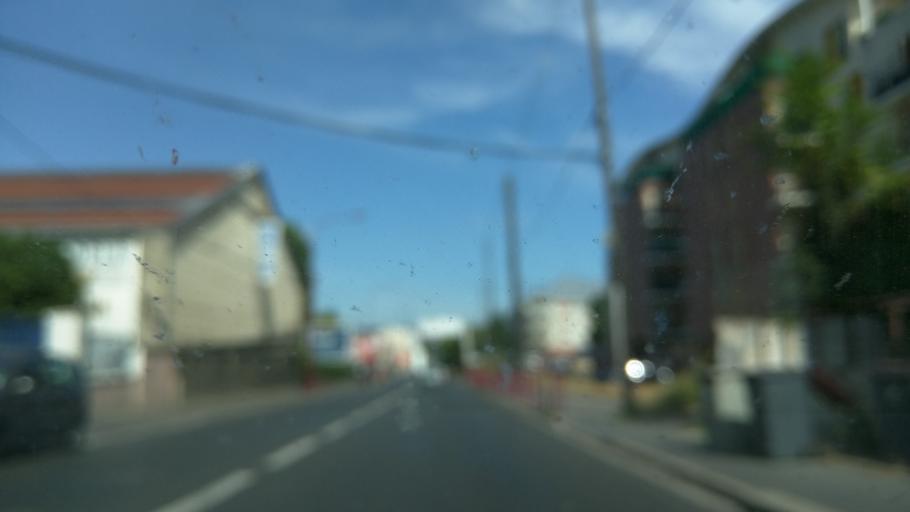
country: FR
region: Ile-de-France
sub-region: Departement du Val-d'Oise
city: Bezons
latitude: 48.9382
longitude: 2.2071
